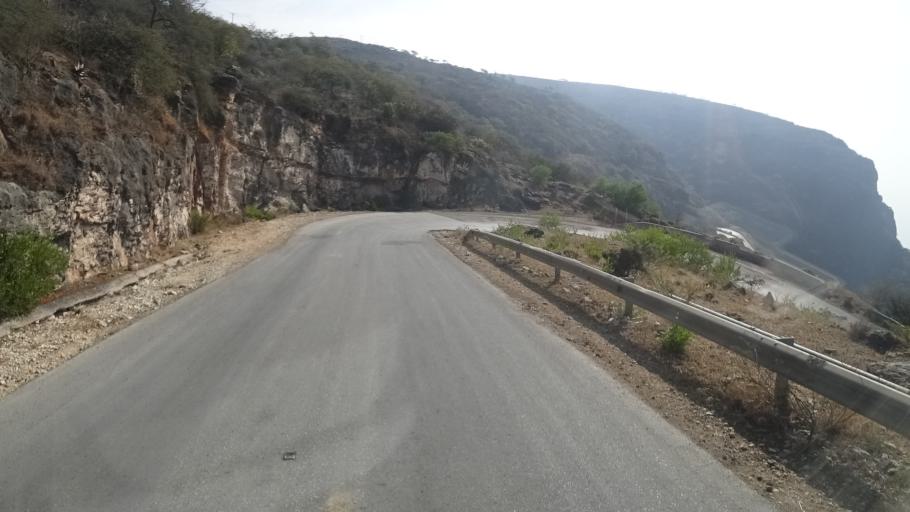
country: YE
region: Al Mahrah
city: Hawf
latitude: 16.7090
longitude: 53.1444
